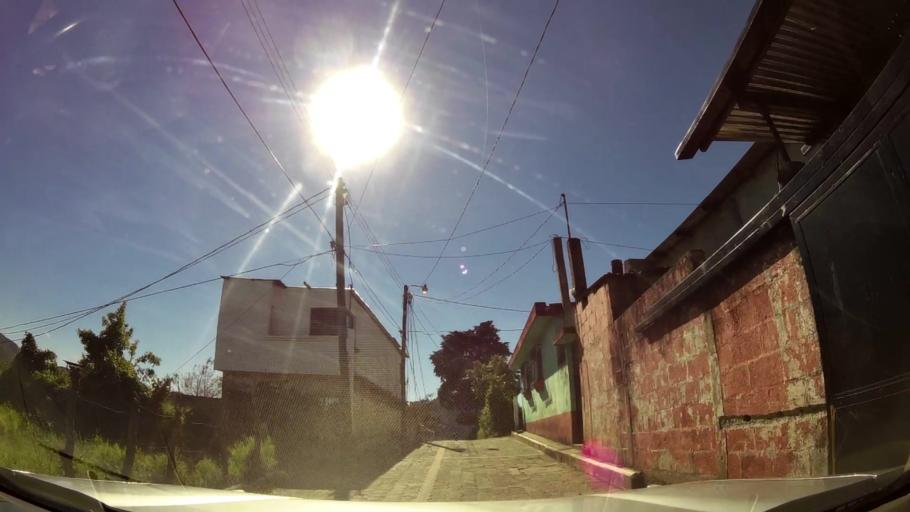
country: GT
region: Guatemala
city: Fraijanes
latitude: 14.4614
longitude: -90.4359
